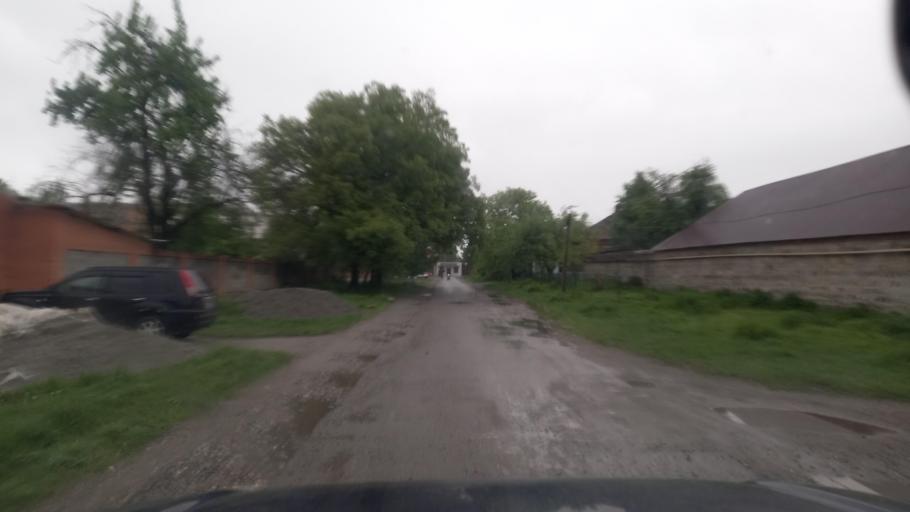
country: RU
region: North Ossetia
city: Alagir
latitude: 43.0457
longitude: 44.2225
